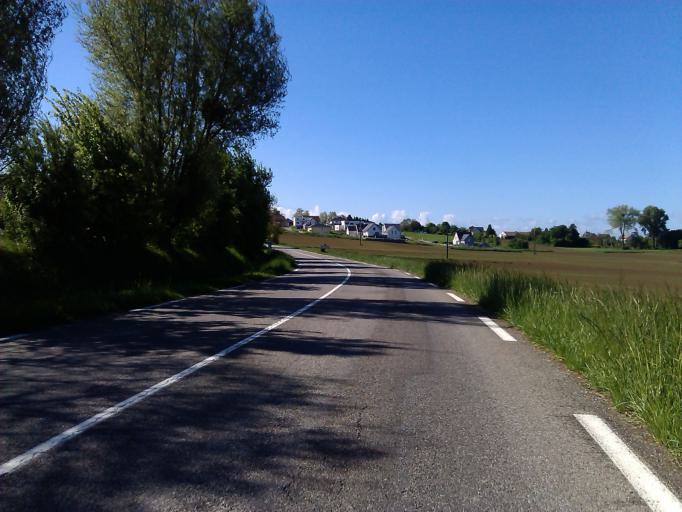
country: FR
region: Alsace
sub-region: Departement du Haut-Rhin
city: Heimsbrunn
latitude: 47.7123
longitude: 7.2249
